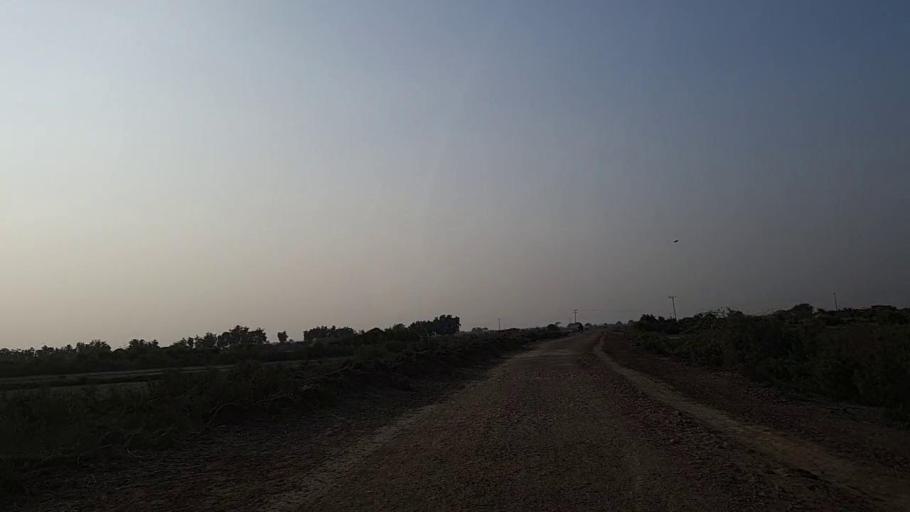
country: PK
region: Sindh
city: Thatta
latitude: 24.6930
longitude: 67.7871
